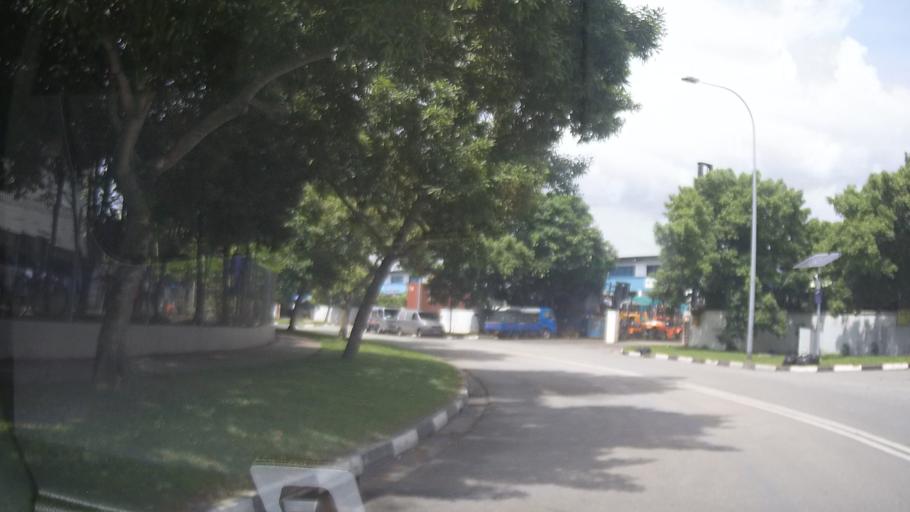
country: MY
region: Johor
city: Johor Bahru
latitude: 1.4357
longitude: 103.7456
